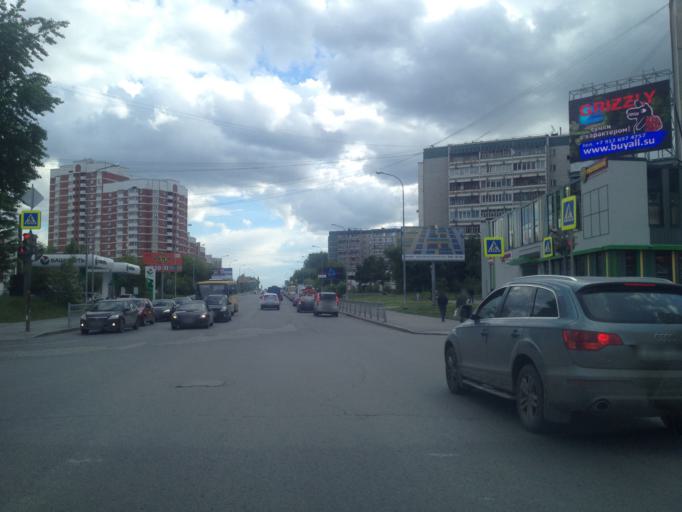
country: RU
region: Sverdlovsk
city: Yekaterinburg
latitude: 56.8537
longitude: 60.5724
